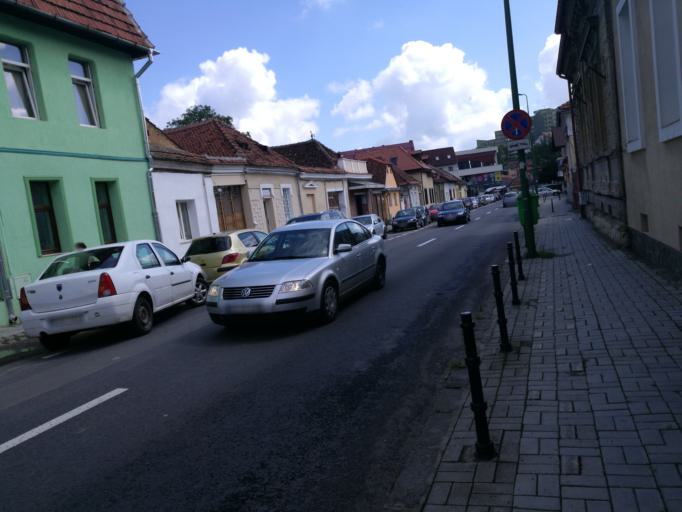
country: RO
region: Brasov
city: Brasov
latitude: 45.6544
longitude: 25.5905
